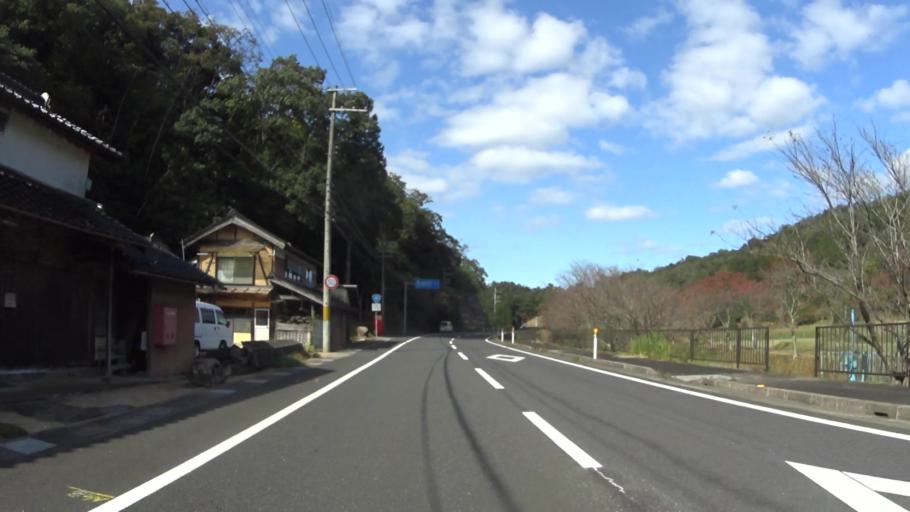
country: JP
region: Hyogo
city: Toyooka
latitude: 35.5629
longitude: 134.9784
